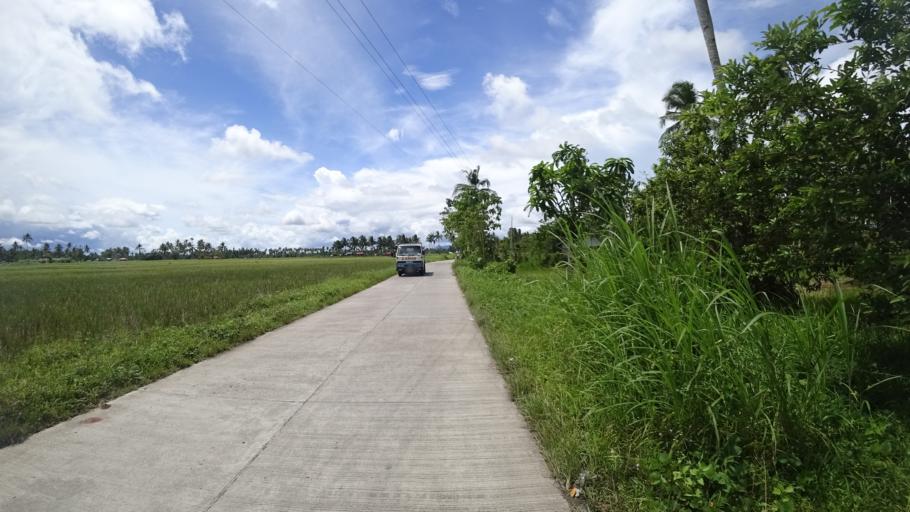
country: PH
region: Eastern Visayas
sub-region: Province of Leyte
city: Alangalang
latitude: 11.2233
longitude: 124.8458
